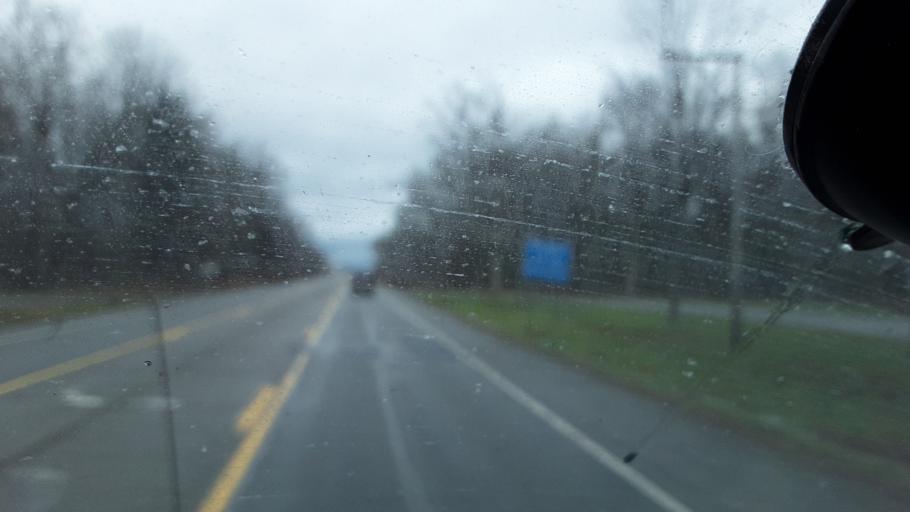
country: US
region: New York
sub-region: Cattaraugus County
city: Yorkshire
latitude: 42.5246
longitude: -78.4785
